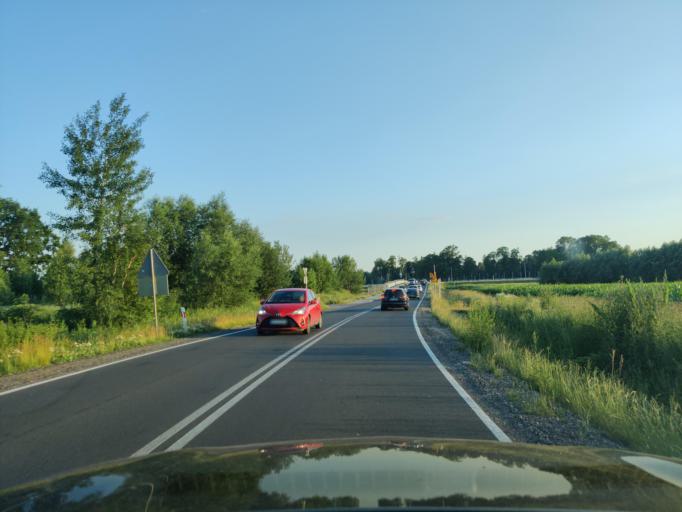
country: PL
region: Masovian Voivodeship
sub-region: Powiat plonski
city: Baboszewo
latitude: 52.7068
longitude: 20.3380
